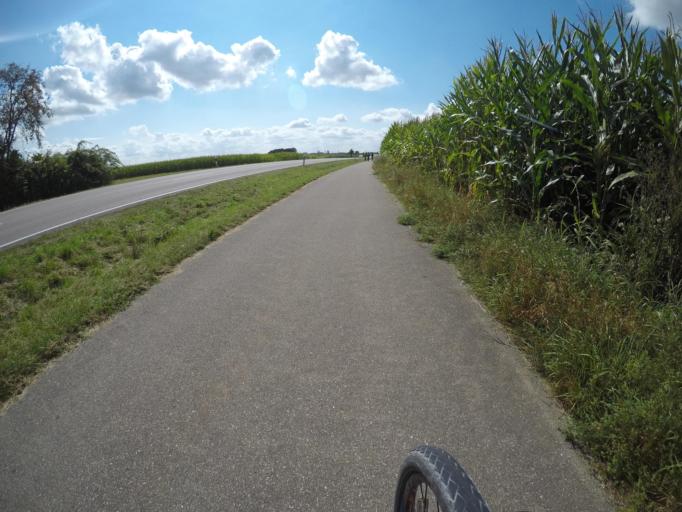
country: DE
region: Bavaria
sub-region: Swabia
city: Dillingen an der Donau
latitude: 48.6090
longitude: 10.5023
